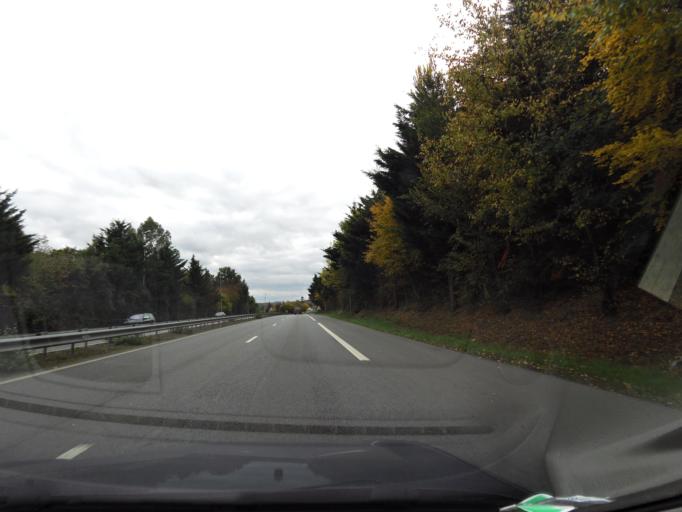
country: FR
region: Brittany
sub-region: Departement d'Ille-et-Vilaine
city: Vern-sur-Seiche
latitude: 48.0472
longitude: -1.6084
